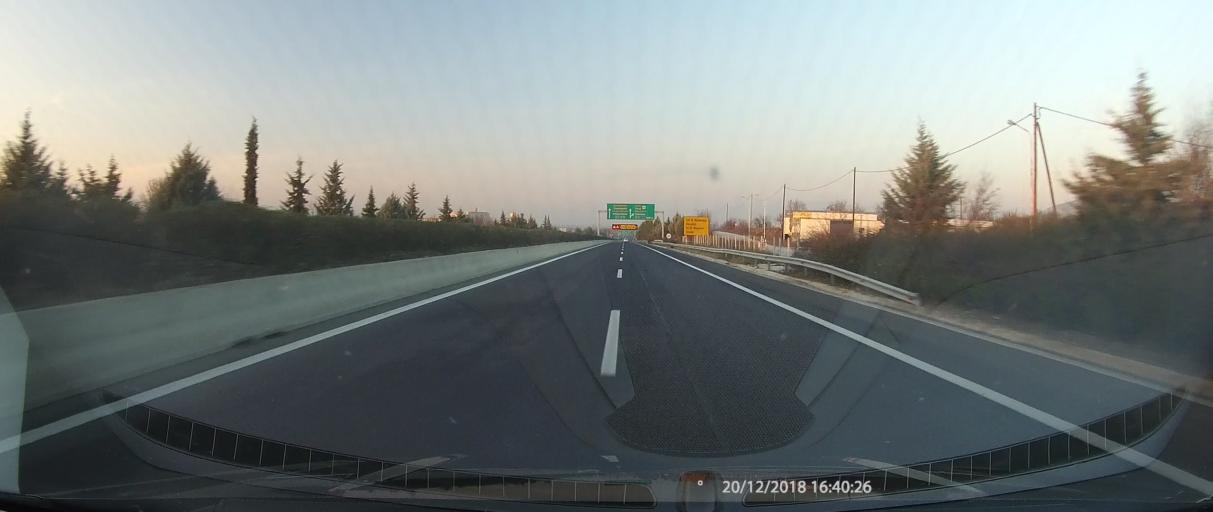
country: GR
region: Thessaly
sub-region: Nomos Magnisias
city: Velestino
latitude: 39.3749
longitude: 22.7700
